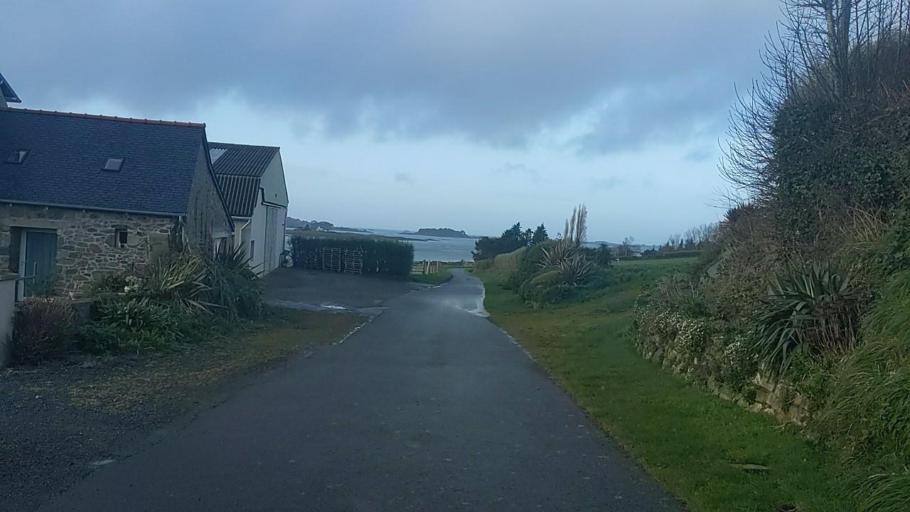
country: FR
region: Brittany
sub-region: Departement des Cotes-d'Armor
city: Plougrescant
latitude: 48.8242
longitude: -3.1966
